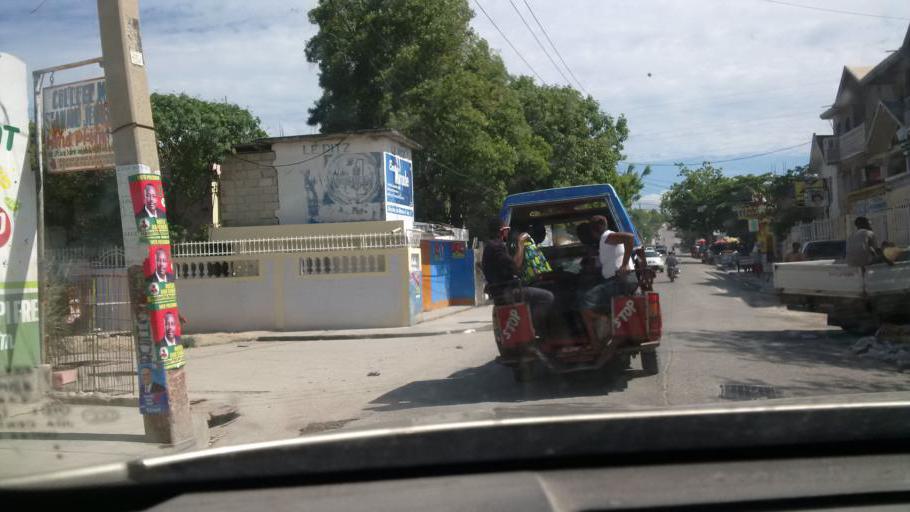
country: HT
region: Ouest
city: Delmas 73
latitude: 18.5601
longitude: -72.3017
